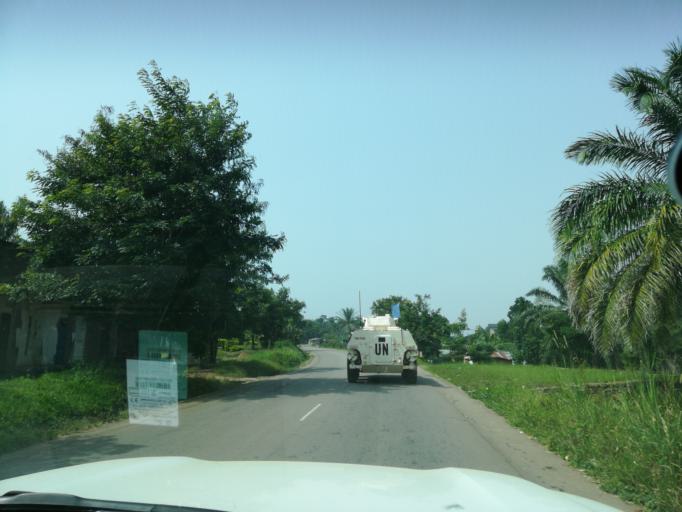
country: CD
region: Nord Kivu
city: Beni
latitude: 0.5223
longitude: 29.4945
